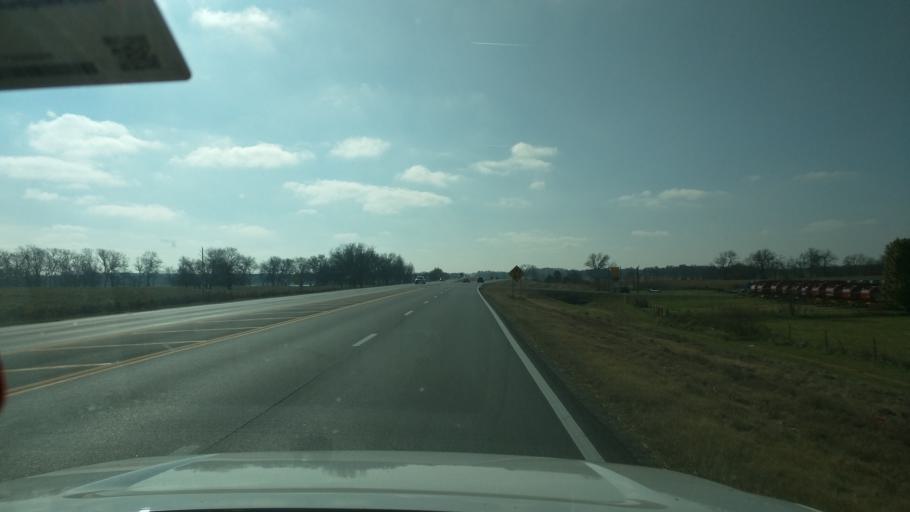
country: US
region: Oklahoma
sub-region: Washington County
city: Bartlesville
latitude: 36.6691
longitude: -95.9353
